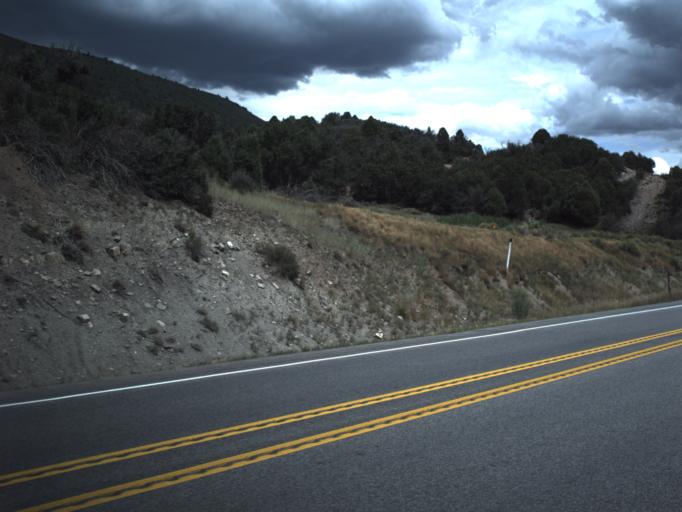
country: US
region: Utah
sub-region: Carbon County
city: Helper
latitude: 39.9342
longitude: -111.1285
